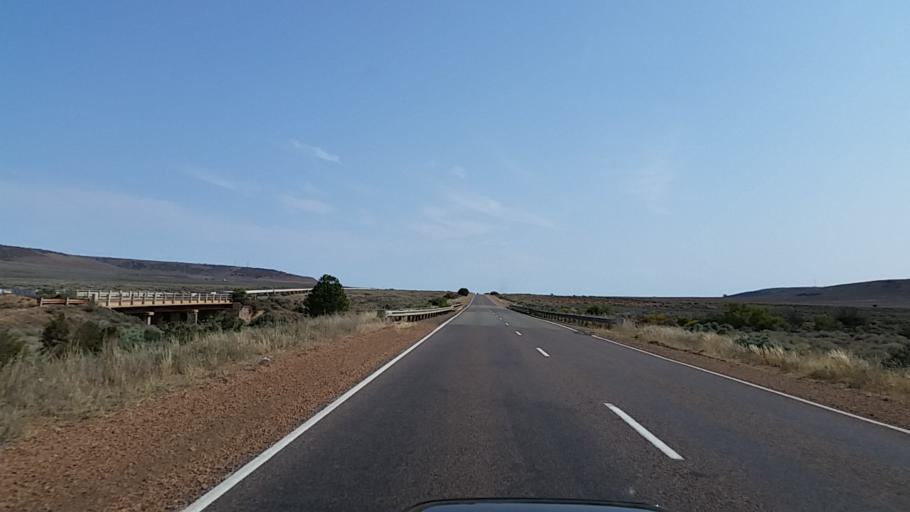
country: AU
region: South Australia
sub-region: Port Augusta
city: Port Augusta West
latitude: -32.5869
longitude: 137.6136
